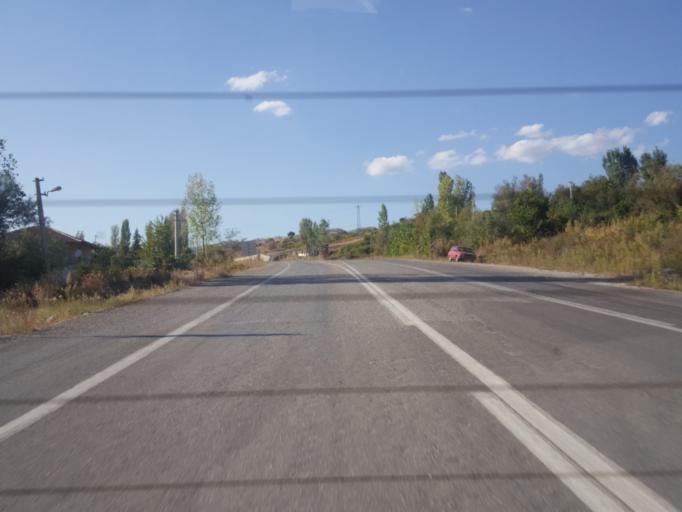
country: TR
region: Amasya
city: Tasova
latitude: 40.7624
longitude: 36.2821
